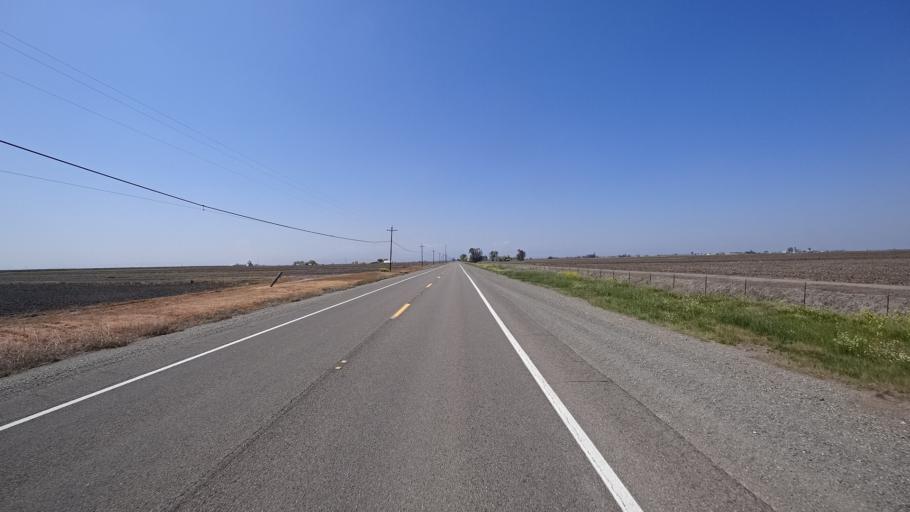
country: US
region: California
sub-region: Glenn County
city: Willows
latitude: 39.5218
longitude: -122.0969
